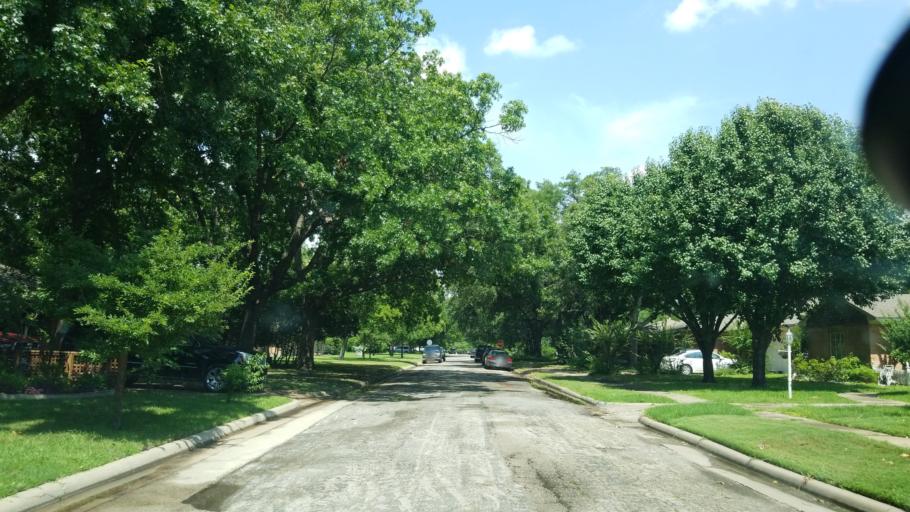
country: US
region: Texas
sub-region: Dallas County
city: Farmers Branch
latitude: 32.8781
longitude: -96.8690
